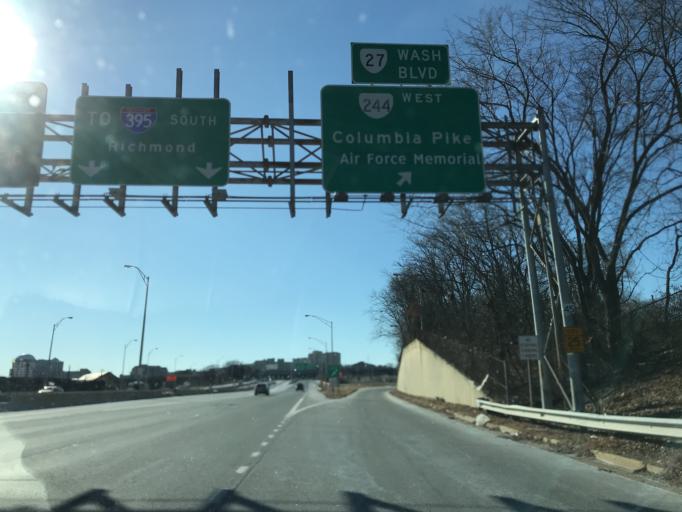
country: US
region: Washington, D.C.
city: Washington, D.C.
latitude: 38.8722
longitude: -77.0593
